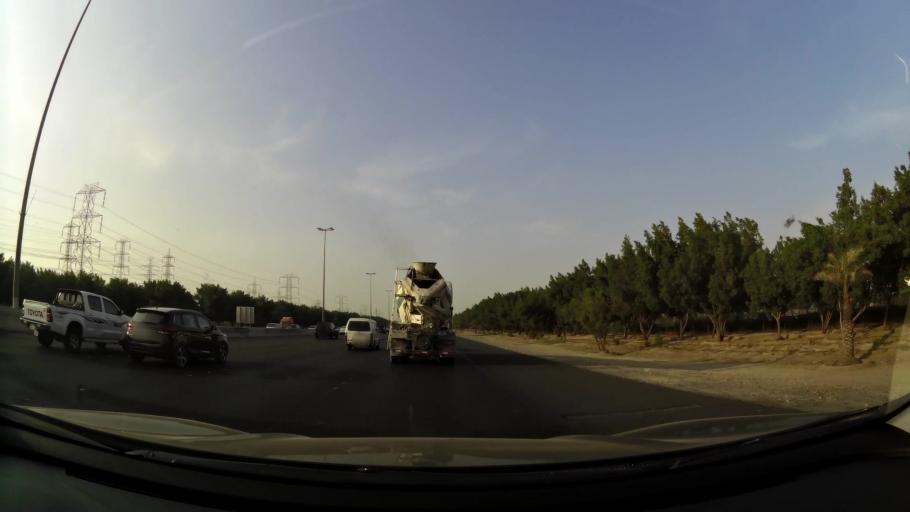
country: KW
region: Mubarak al Kabir
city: Sabah as Salim
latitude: 29.2257
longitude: 48.0542
